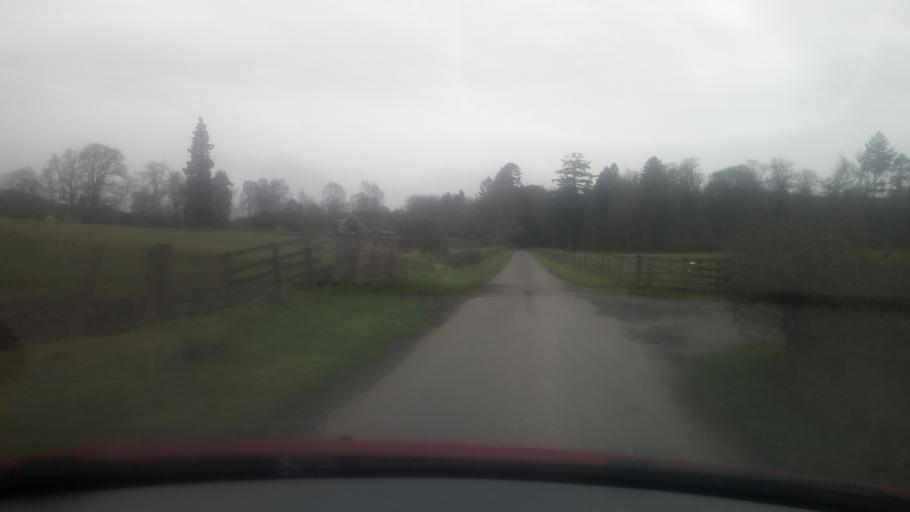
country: GB
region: Scotland
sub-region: The Scottish Borders
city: Jedburgh
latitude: 55.4481
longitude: -2.6401
